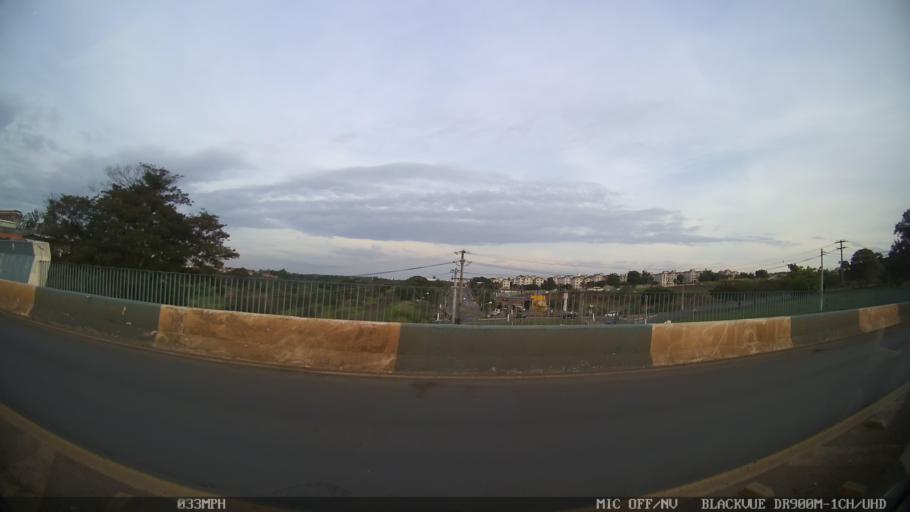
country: BR
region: Sao Paulo
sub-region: Limeira
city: Limeira
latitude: -22.5882
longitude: -47.3827
